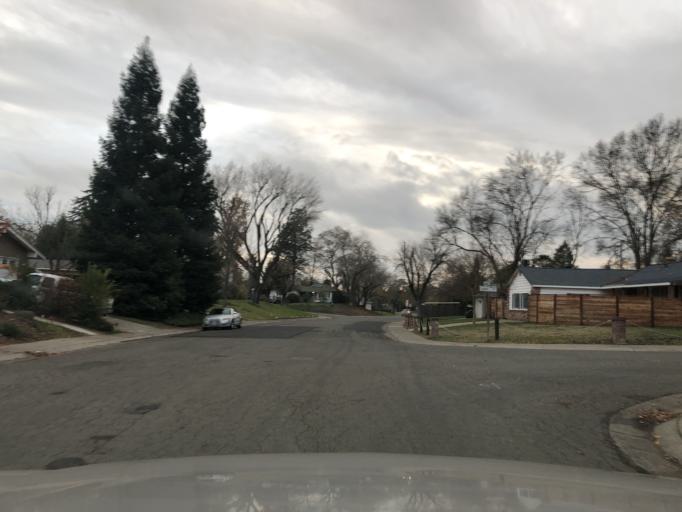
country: US
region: California
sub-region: Sacramento County
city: Fair Oaks
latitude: 38.6575
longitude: -121.3113
